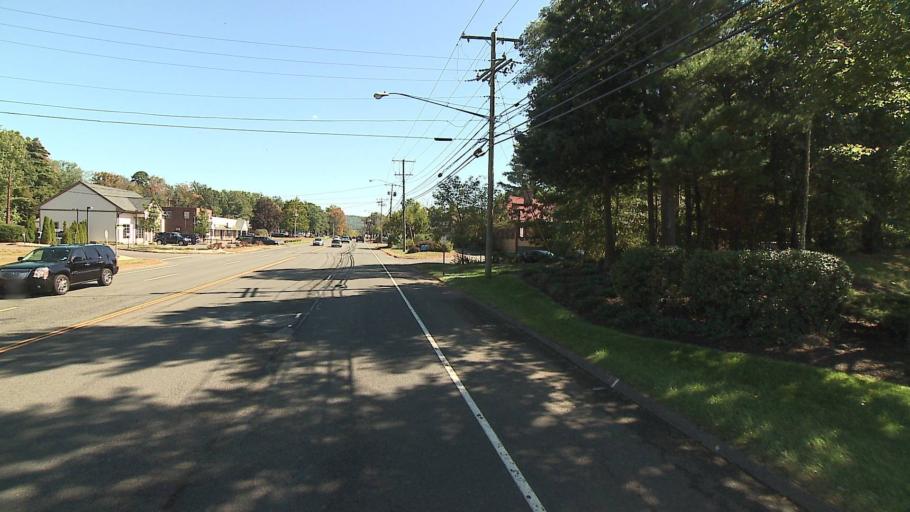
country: US
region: Connecticut
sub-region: Hartford County
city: Weatogue
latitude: 41.8120
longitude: -72.8514
